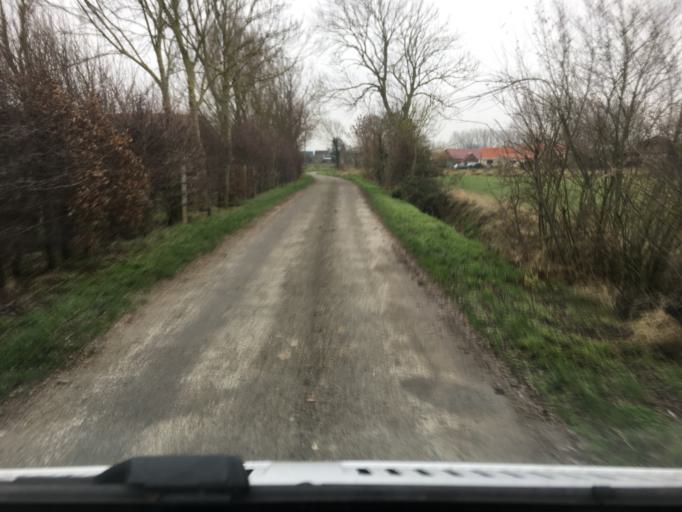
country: FR
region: Picardie
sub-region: Departement de la Somme
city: Pende
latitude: 50.1745
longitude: 1.5449
